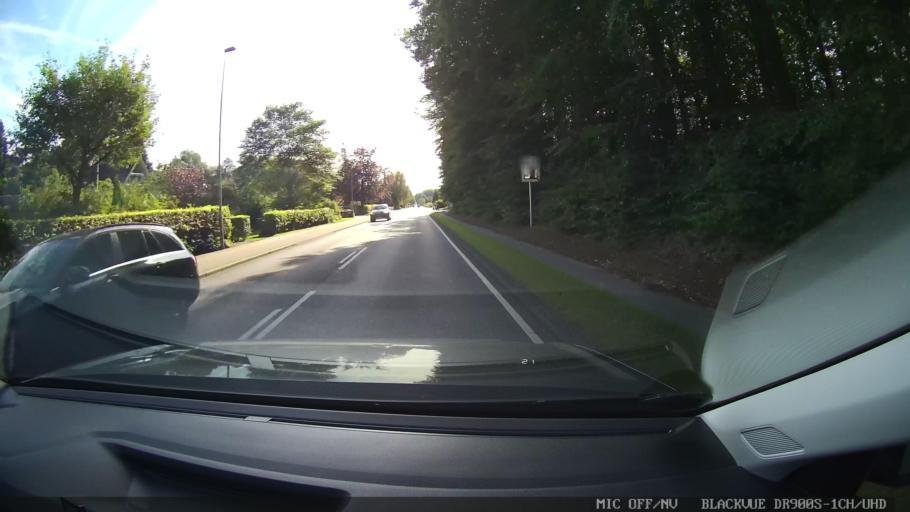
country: DK
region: North Denmark
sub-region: Mariagerfjord Kommune
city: Hadsund
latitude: 56.7219
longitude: 10.0999
